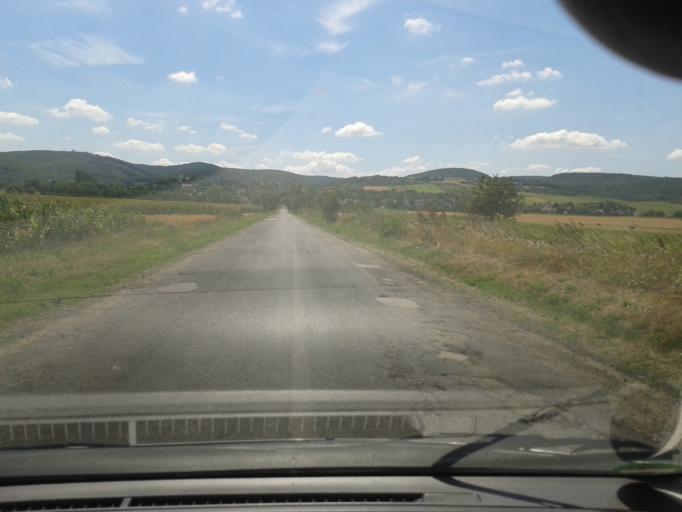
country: HU
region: Komarom-Esztergom
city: Pilismarot
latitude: 47.7941
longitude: 18.8827
